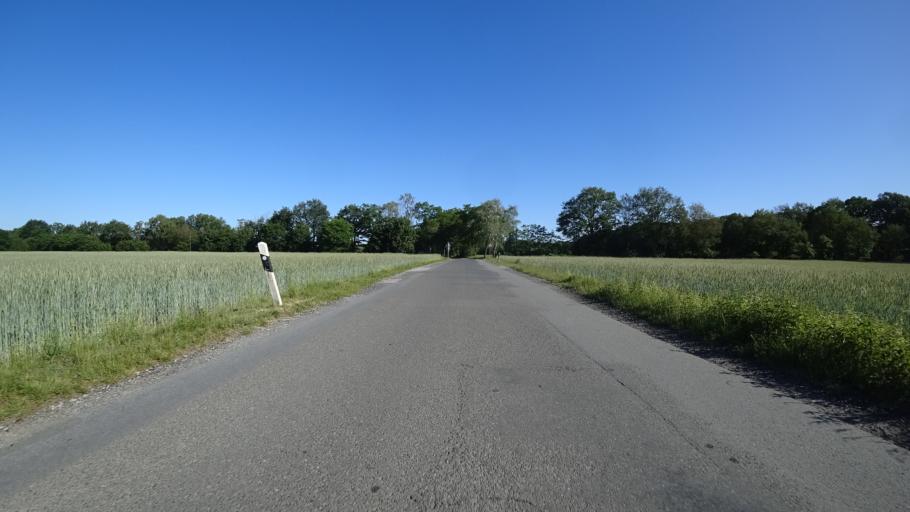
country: DE
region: North Rhine-Westphalia
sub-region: Regierungsbezirk Detmold
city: Guetersloh
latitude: 51.9089
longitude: 8.3307
